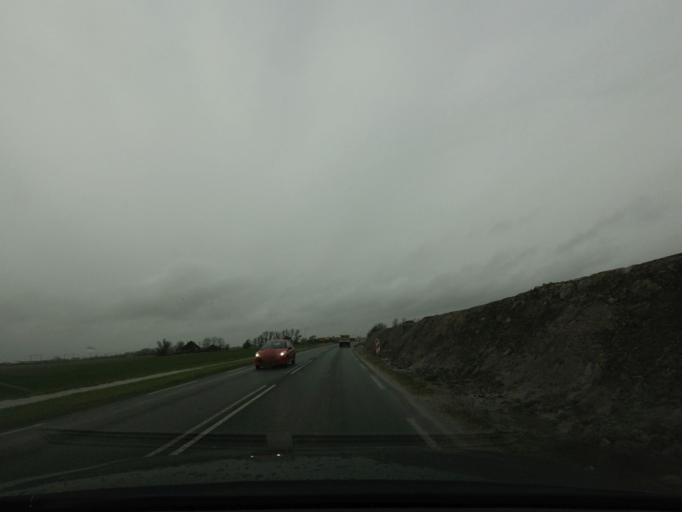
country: NL
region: North Holland
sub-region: Gemeente Schagen
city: Schagen
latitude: 52.7493
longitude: 4.8320
